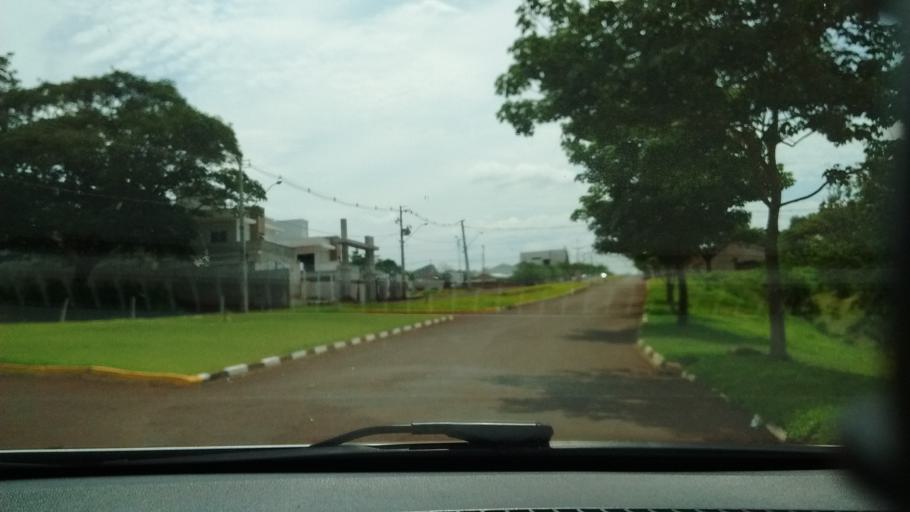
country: BR
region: Parana
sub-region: Corbelia
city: Corbelia
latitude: -24.5498
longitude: -52.9802
